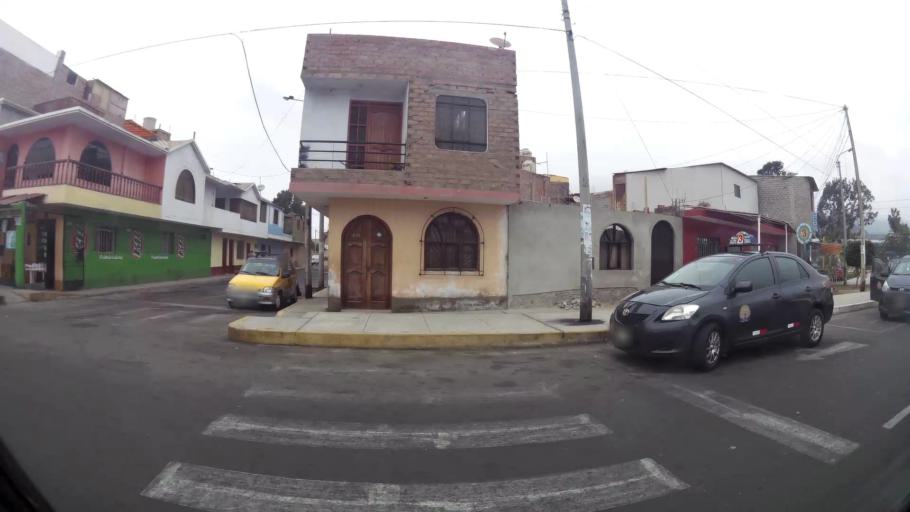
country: PE
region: Ancash
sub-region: Provincia de Santa
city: Chimbote
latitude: -9.0672
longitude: -78.5975
